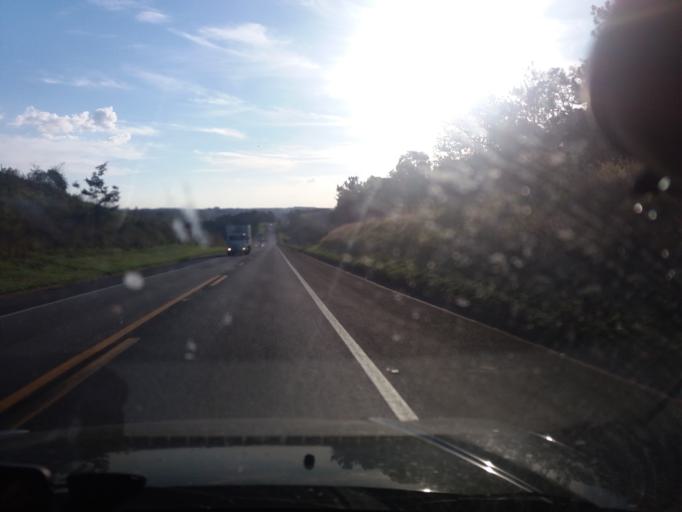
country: BR
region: Sao Paulo
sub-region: Buri
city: Buri
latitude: -23.9362
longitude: -48.6252
